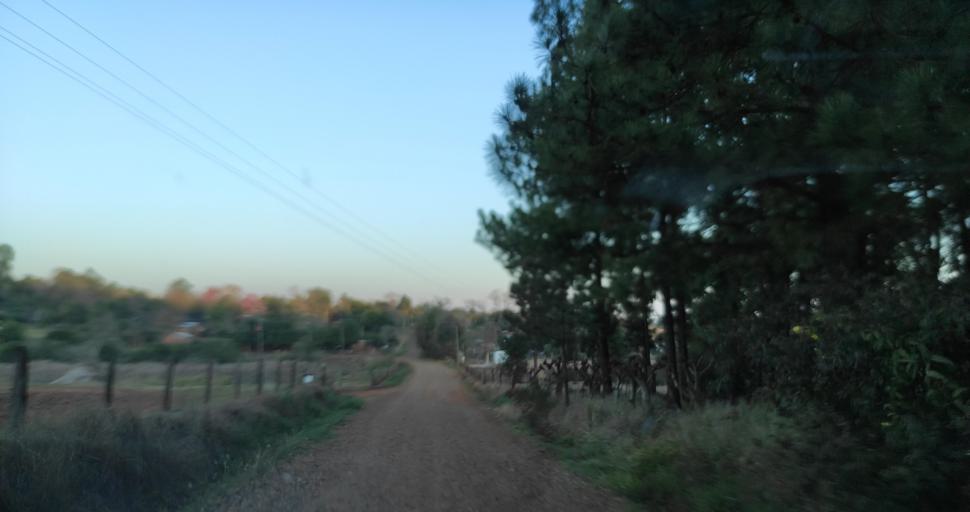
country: AR
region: Misiones
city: Capiovi
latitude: -26.8908
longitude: -55.0752
